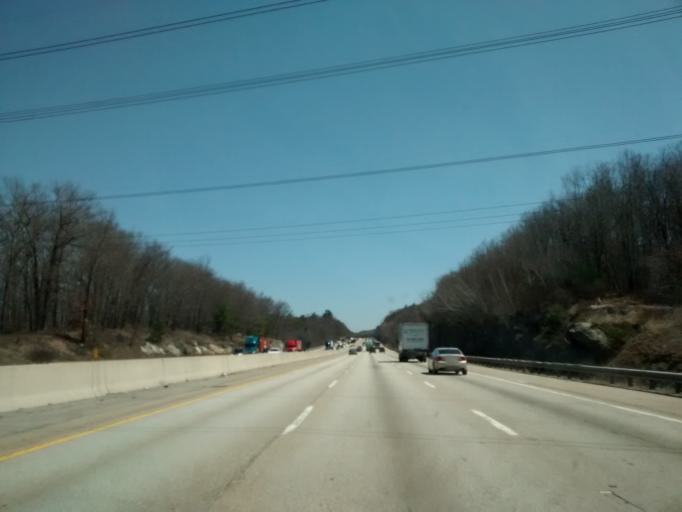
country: US
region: Massachusetts
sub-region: Worcester County
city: Millbury
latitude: 42.2227
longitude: -71.7342
